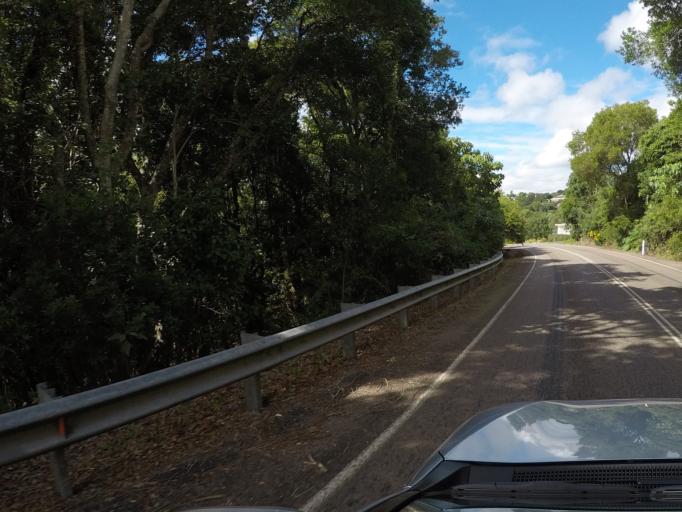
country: AU
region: Queensland
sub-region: Sunshine Coast
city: Nambour
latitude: -26.6396
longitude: 152.8702
